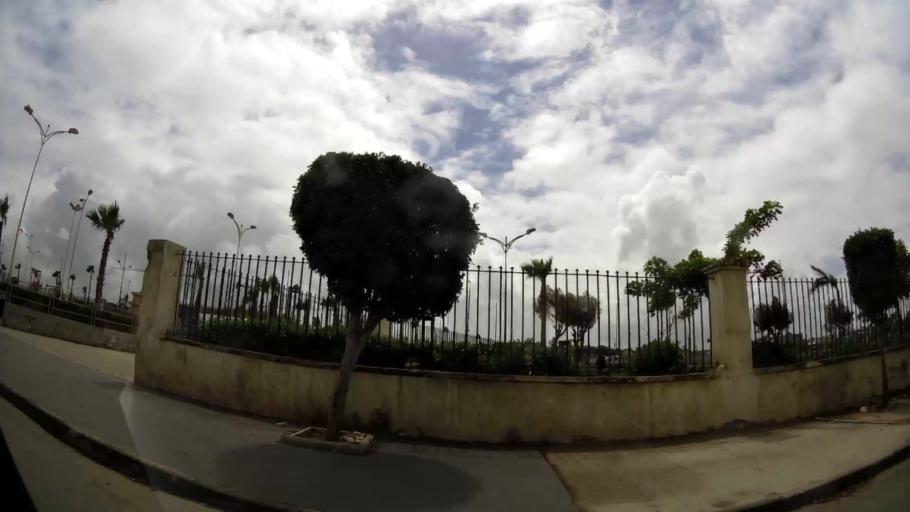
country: MA
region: Grand Casablanca
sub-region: Mediouna
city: Tit Mellil
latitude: 33.6018
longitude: -7.5148
